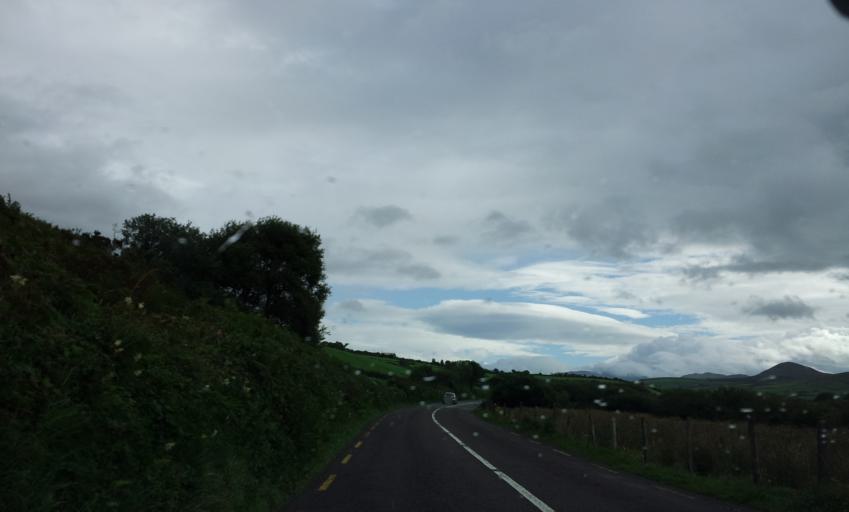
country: IE
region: Munster
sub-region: Ciarrai
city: Dingle
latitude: 52.1451
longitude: -10.0807
